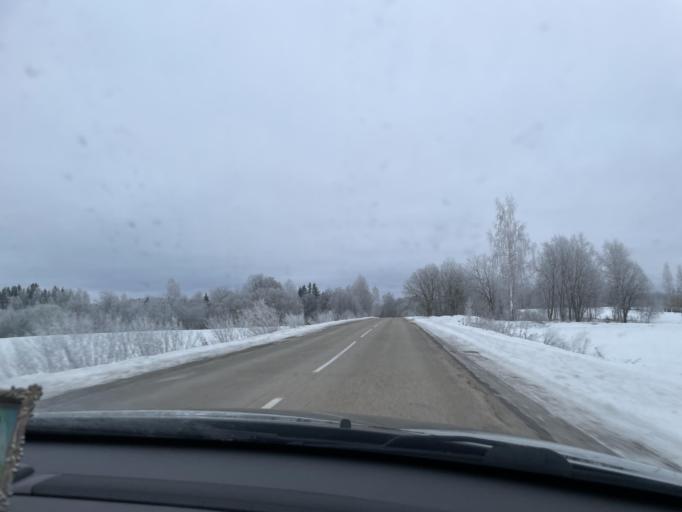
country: LV
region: Rezekne
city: Rezekne
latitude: 56.4391
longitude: 27.5123
